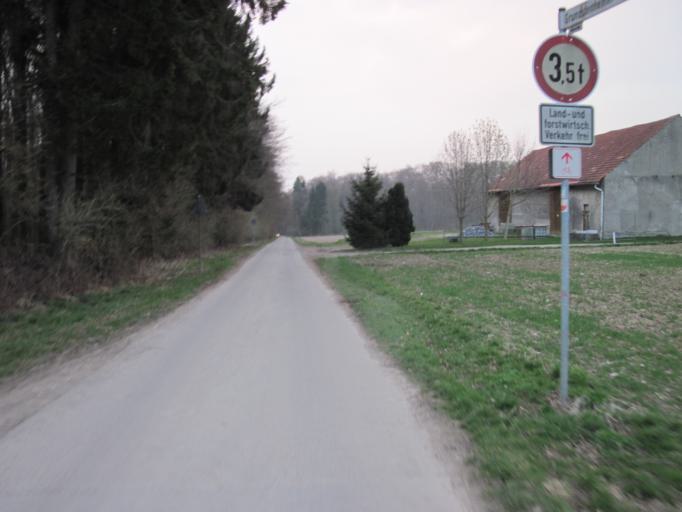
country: DE
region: North Rhine-Westphalia
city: Lichtenau
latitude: 51.6792
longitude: 8.8570
